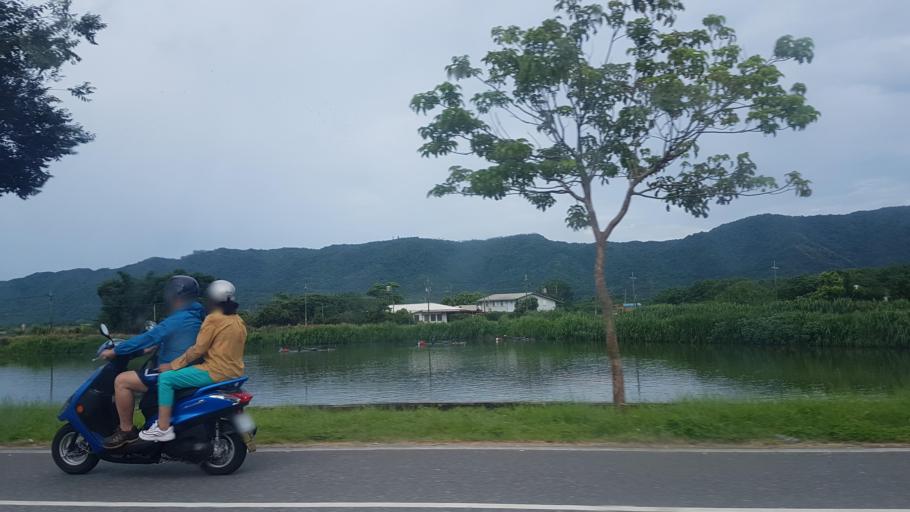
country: TW
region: Taiwan
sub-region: Hualien
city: Hualian
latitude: 23.8844
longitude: 121.5447
